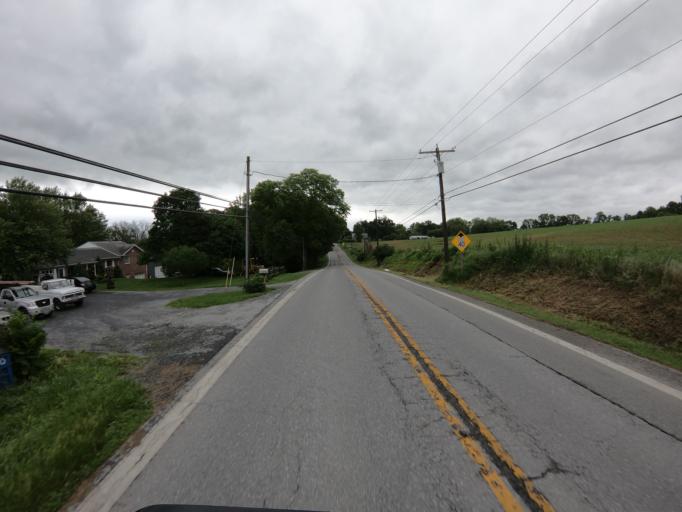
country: US
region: Maryland
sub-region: Frederick County
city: Myersville
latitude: 39.4634
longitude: -77.5873
